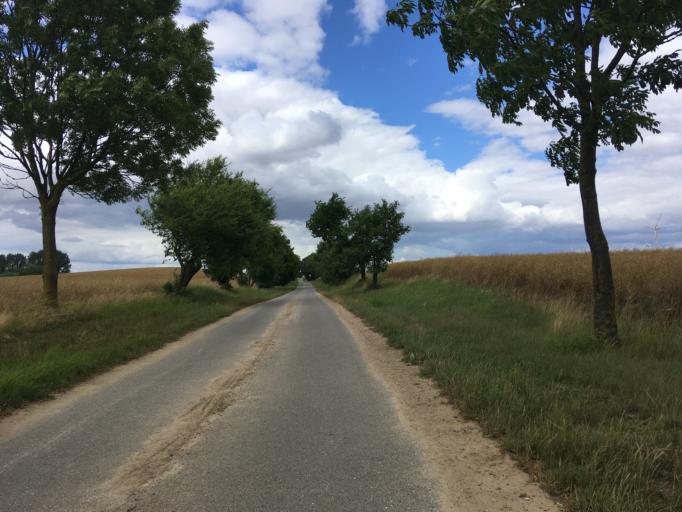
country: DE
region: Brandenburg
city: Gramzow
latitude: 53.2576
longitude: 14.0141
